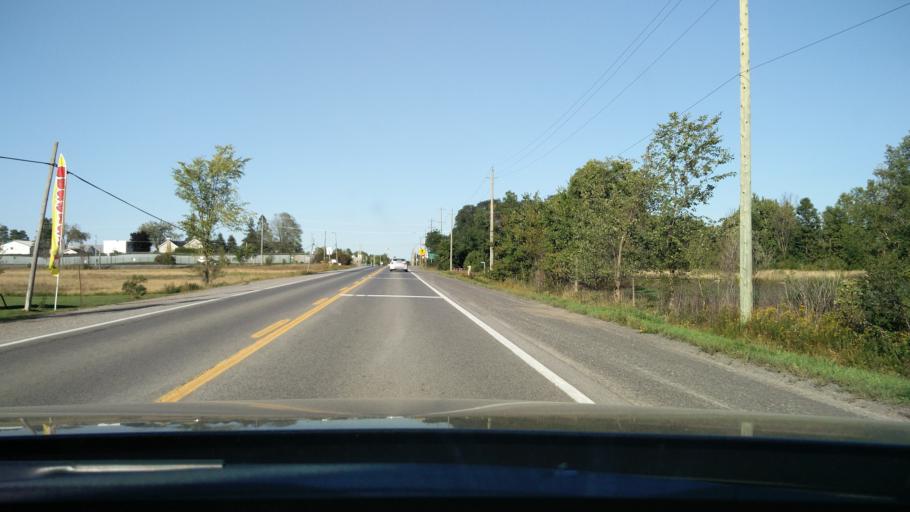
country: CA
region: Ontario
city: Carleton Place
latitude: 45.1258
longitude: -75.9479
